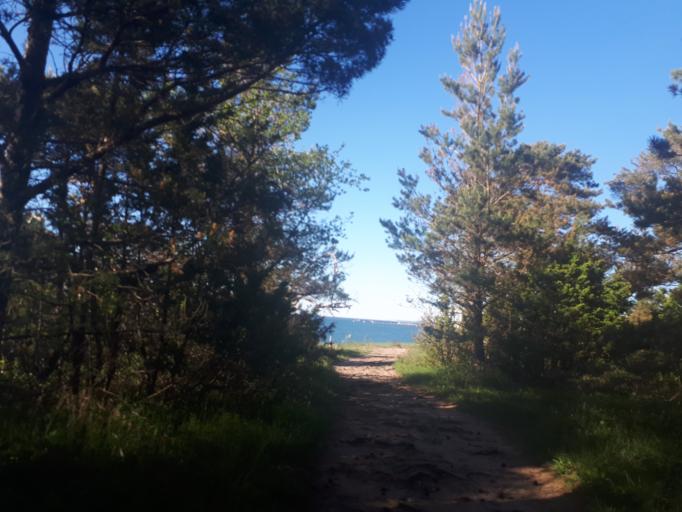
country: SE
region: Gotland
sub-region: Gotland
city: Vibble
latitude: 57.6144
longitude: 18.2519
